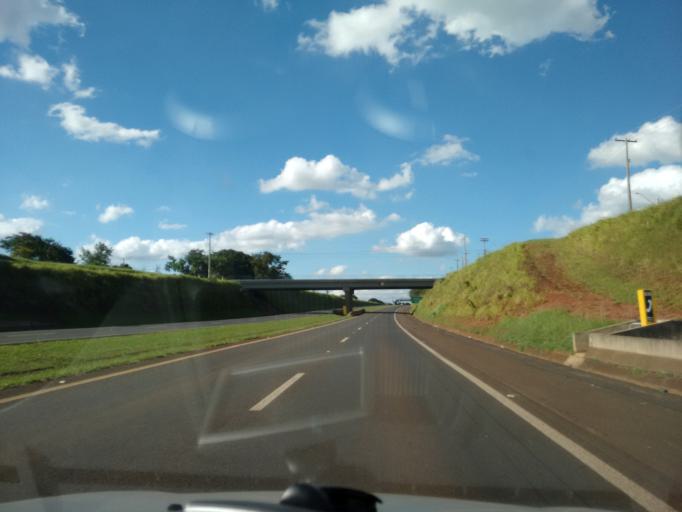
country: BR
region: Sao Paulo
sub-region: Araraquara
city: Araraquara
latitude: -21.8053
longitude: -48.1499
